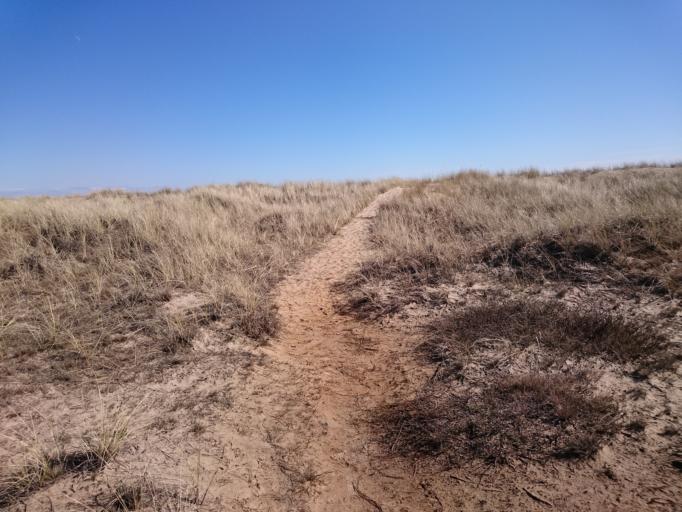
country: DK
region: North Denmark
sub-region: Frederikshavn Kommune
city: Skagen
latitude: 57.6919
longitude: 10.5306
